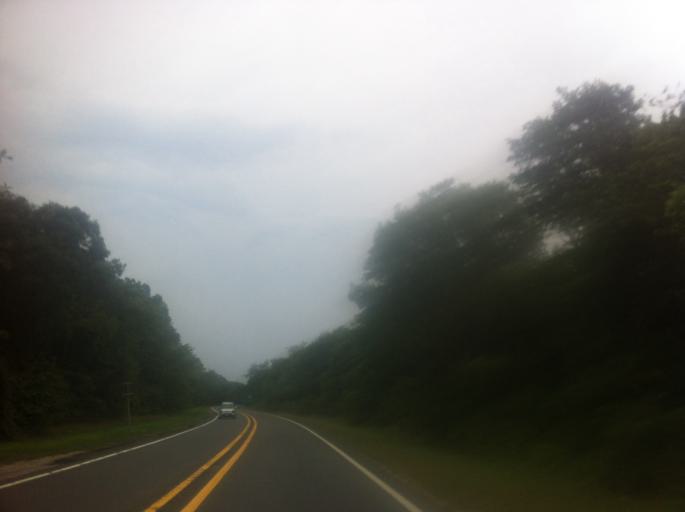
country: US
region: New York
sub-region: Nassau County
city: North Massapequa
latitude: 40.7144
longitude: -73.4577
